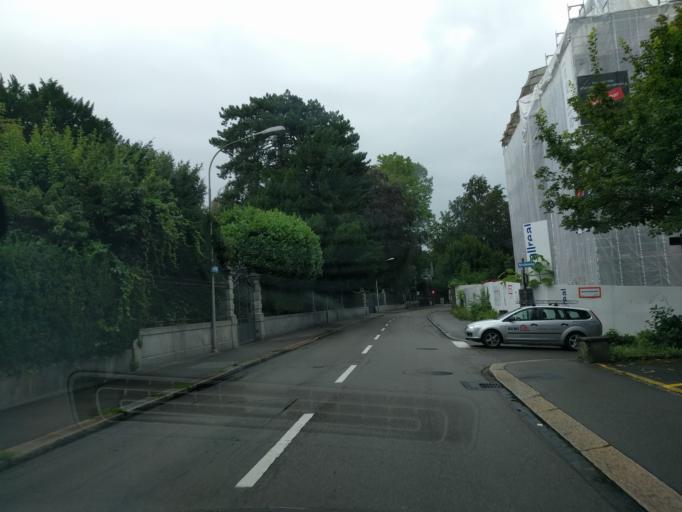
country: CH
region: Zurich
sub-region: Bezirk Zuerich
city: Zuerich (Kreis 8) / Muehlebach
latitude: 47.3617
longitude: 8.5562
